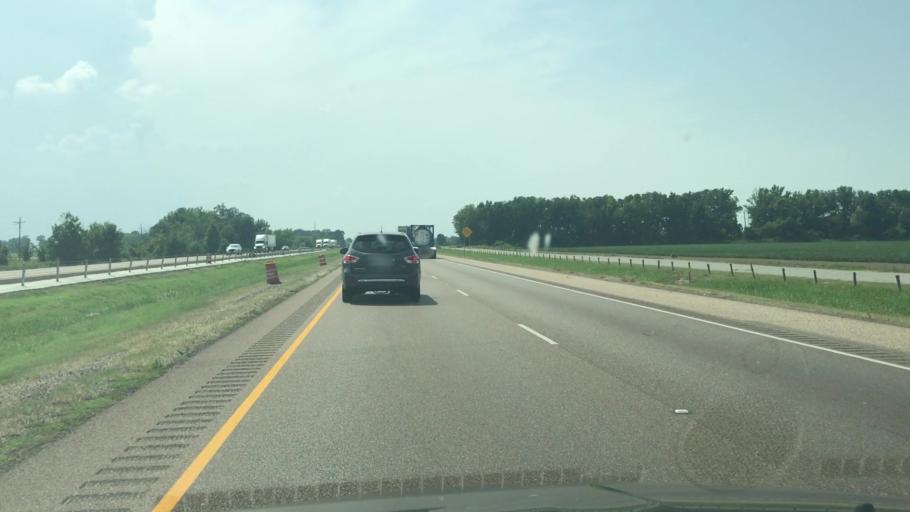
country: US
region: Arkansas
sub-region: Crittenden County
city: West Memphis
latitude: 35.1485
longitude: -90.3336
